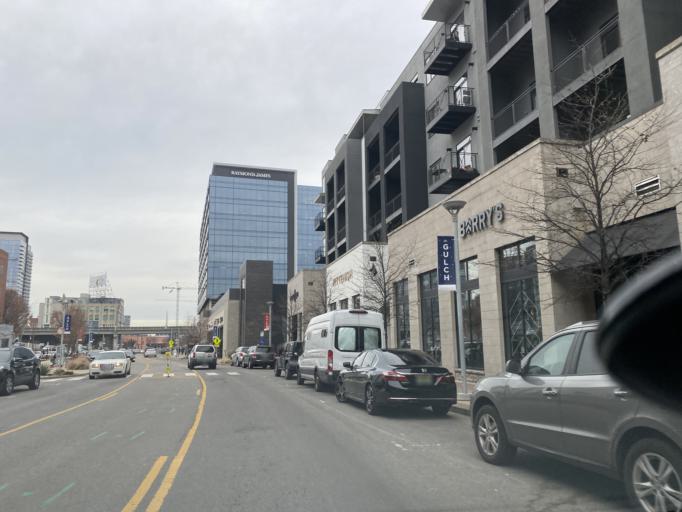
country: US
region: Tennessee
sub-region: Davidson County
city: Nashville
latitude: 36.1532
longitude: -86.7838
